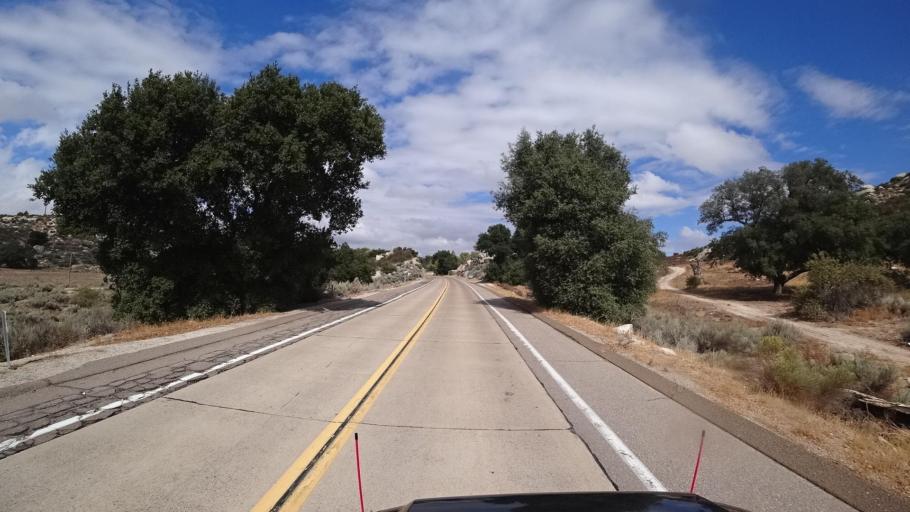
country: US
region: California
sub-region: San Diego County
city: Campo
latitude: 32.6844
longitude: -116.3347
